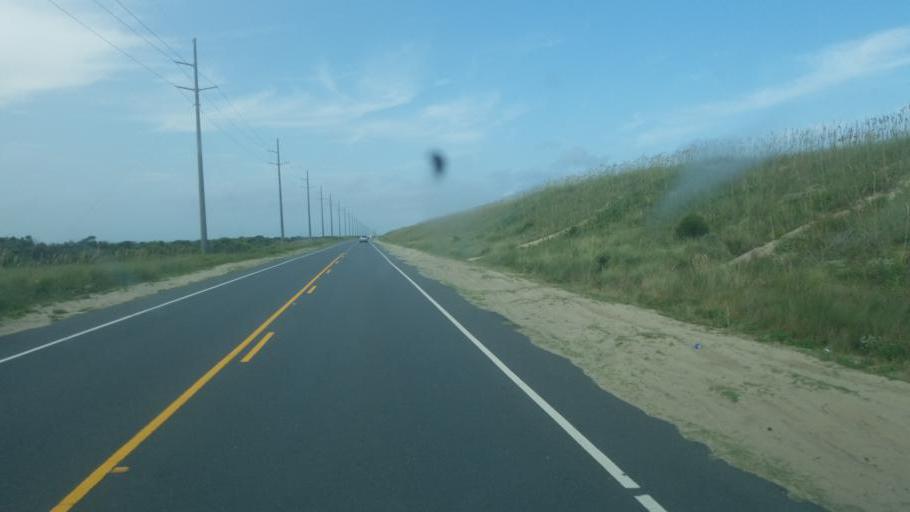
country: US
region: North Carolina
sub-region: Dare County
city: Buxton
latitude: 35.2723
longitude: -75.5184
